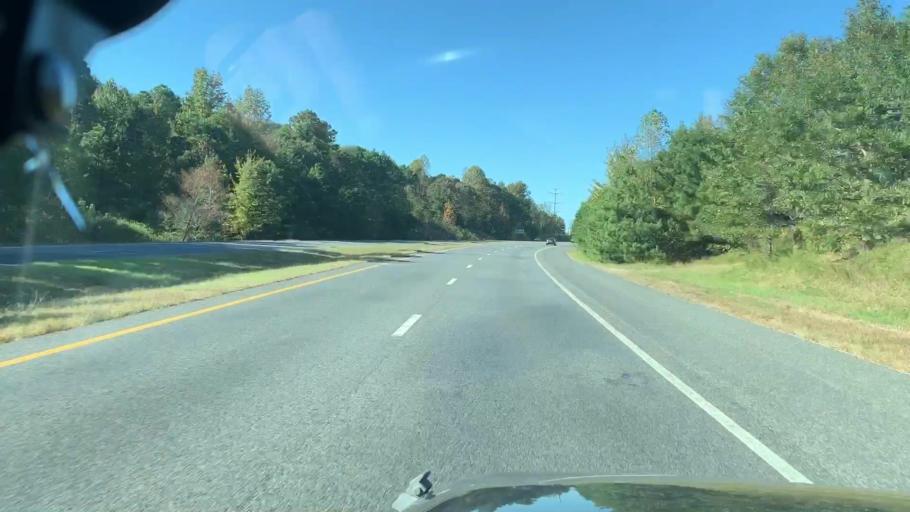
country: US
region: Virginia
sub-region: James City County
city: Williamsburg
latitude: 37.3233
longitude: -76.7535
